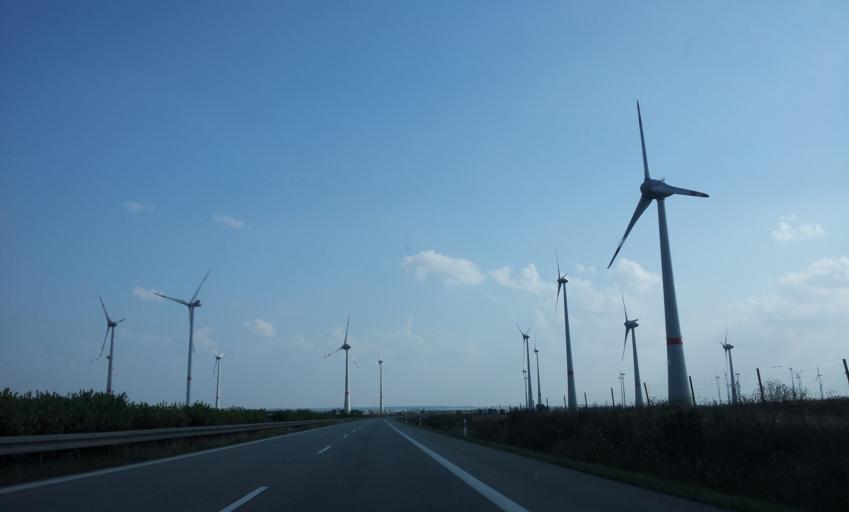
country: DE
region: Mecklenburg-Vorpommern
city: Kessin
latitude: 53.7272
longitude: 13.3340
